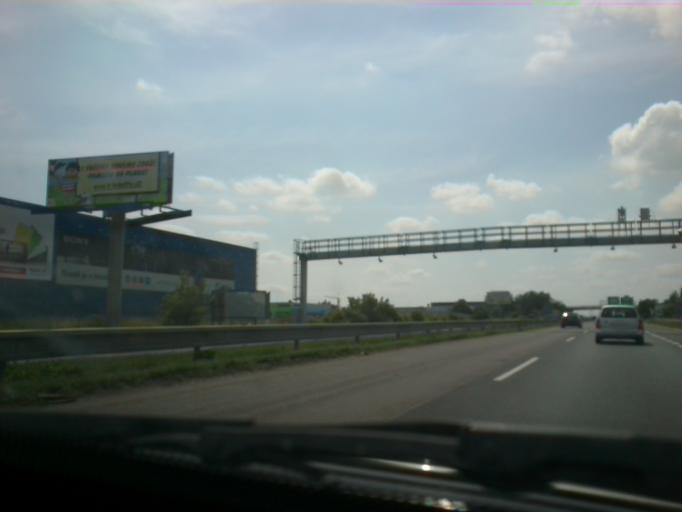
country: CZ
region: Praha
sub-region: Praha 20
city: Horni Pocernice
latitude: 50.1238
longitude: 14.6083
